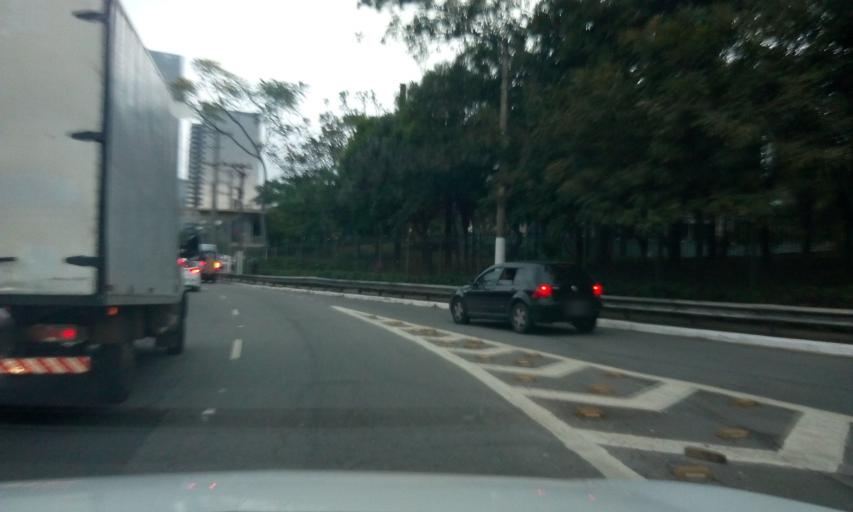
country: BR
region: Sao Paulo
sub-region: Taboao Da Serra
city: Taboao da Serra
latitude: -23.6186
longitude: -46.7023
